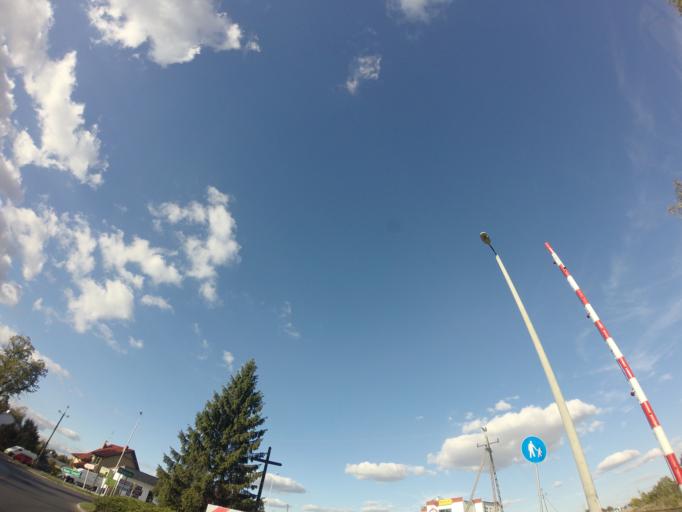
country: PL
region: Greater Poland Voivodeship
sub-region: Powiat grodziski
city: Rakoniewice
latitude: 52.1432
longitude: 16.2745
